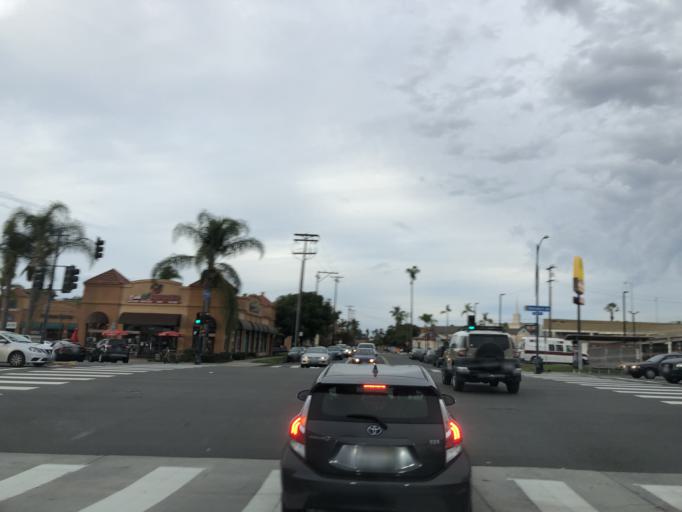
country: US
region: California
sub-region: San Diego County
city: San Diego
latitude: 32.7483
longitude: -117.1512
